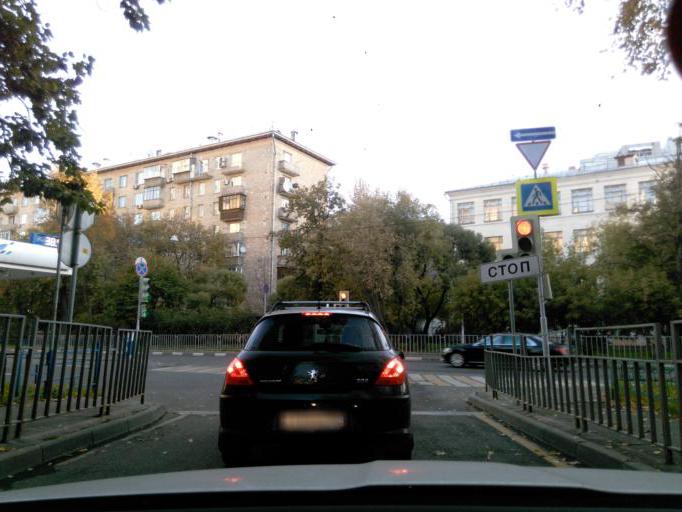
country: RU
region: Moskovskaya
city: Dorogomilovo
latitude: 55.7679
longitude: 37.5870
